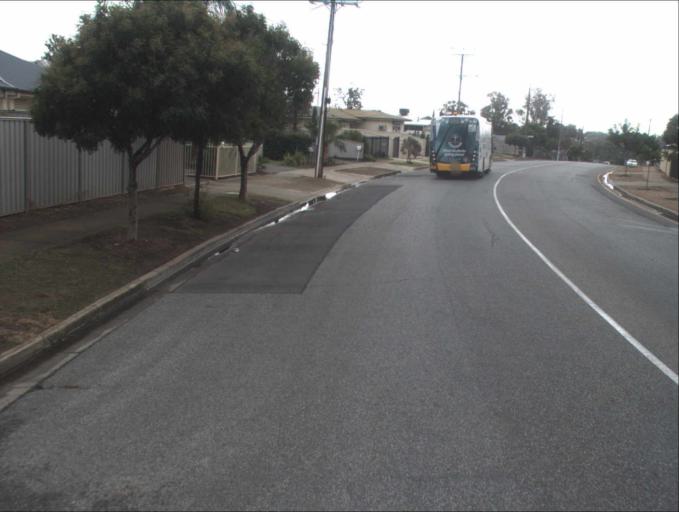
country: AU
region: South Australia
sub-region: Port Adelaide Enfield
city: Gilles Plains
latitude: -34.8483
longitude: 138.6600
